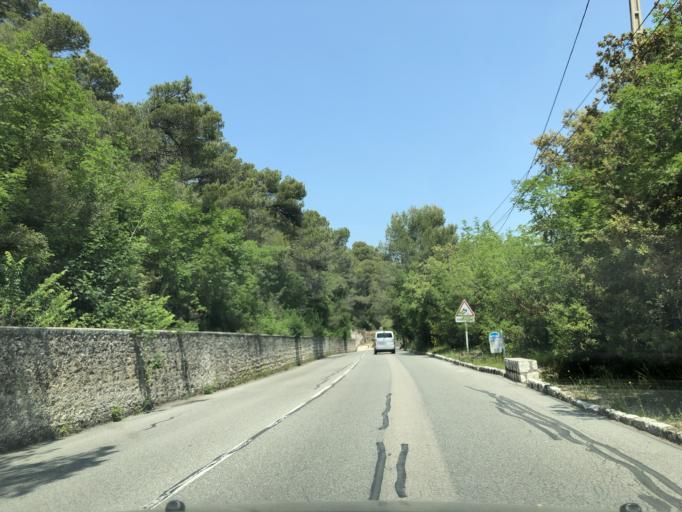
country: FR
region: Provence-Alpes-Cote d'Azur
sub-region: Departement des Alpes-Maritimes
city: La Trinite
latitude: 43.7273
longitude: 7.3033
